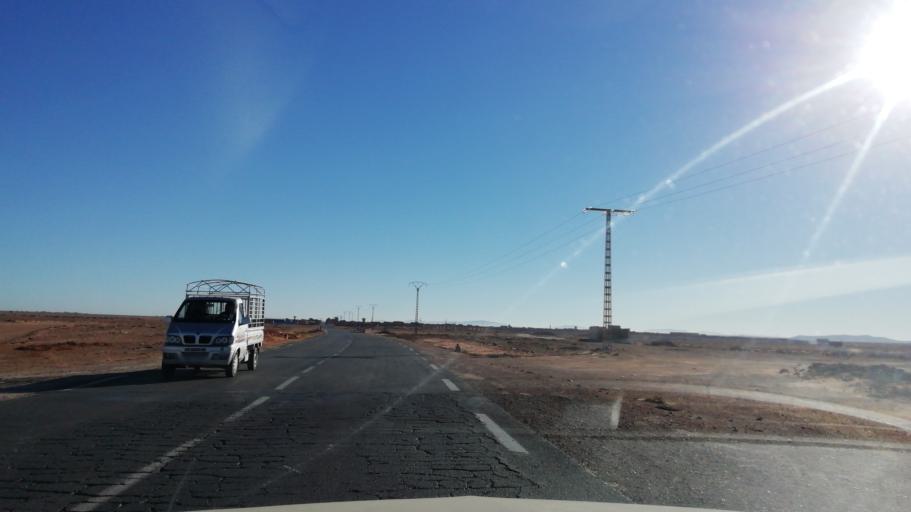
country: DZ
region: El Bayadh
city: El Bayadh
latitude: 33.8537
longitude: 0.6138
